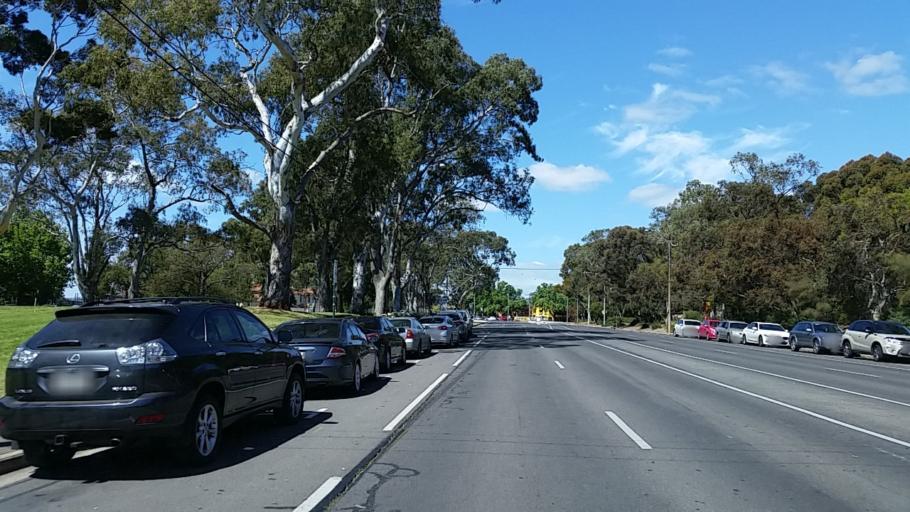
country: AU
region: South Australia
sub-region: Adelaide
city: Adelaide
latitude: -34.9250
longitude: 138.6164
